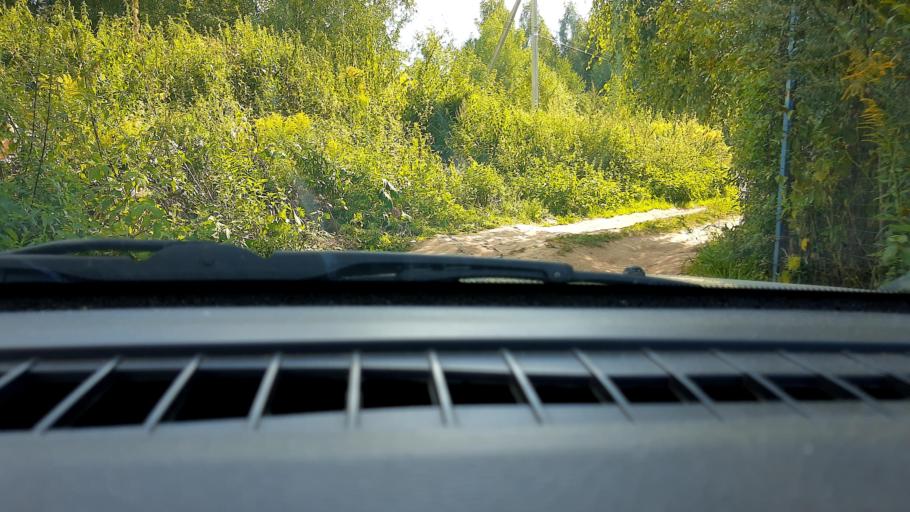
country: RU
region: Nizjnij Novgorod
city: Afonino
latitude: 56.2494
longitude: 44.0670
